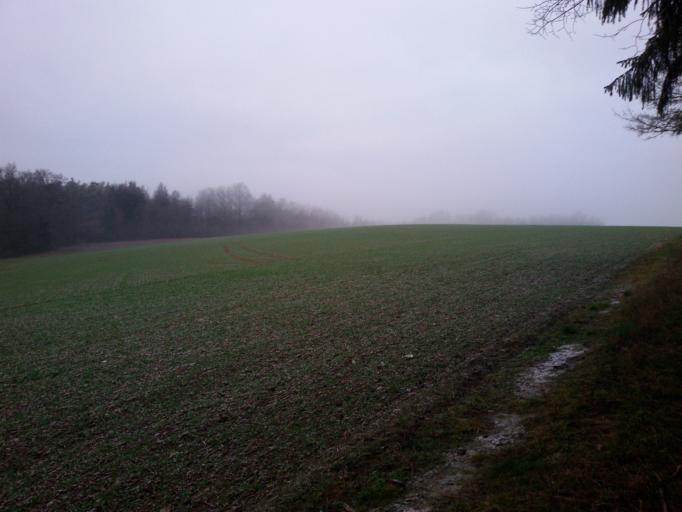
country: DE
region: Bavaria
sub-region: Upper Palatinate
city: Gebenbach
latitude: 49.5135
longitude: 11.8641
